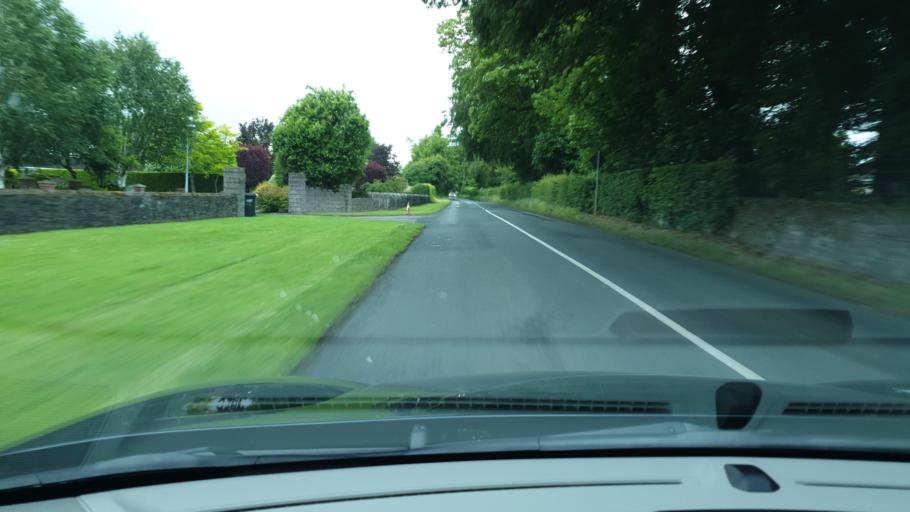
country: IE
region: Leinster
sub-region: An Mhi
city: Navan
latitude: 53.6238
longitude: -6.6664
